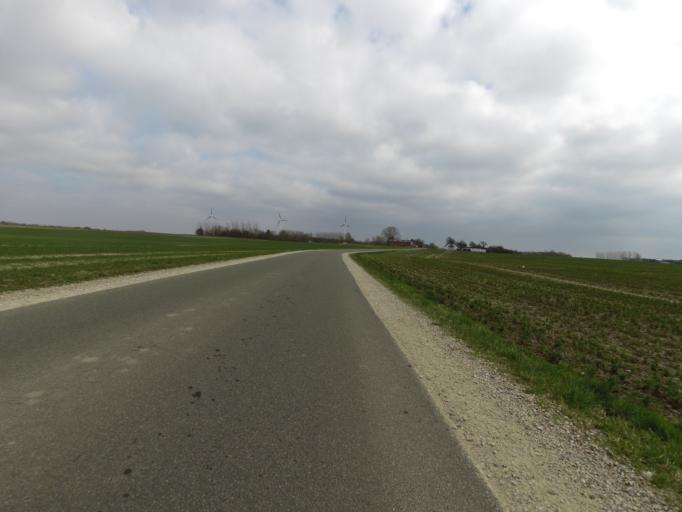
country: DK
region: Central Jutland
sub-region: Holstebro Kommune
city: Holstebro
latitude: 56.4322
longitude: 8.6806
